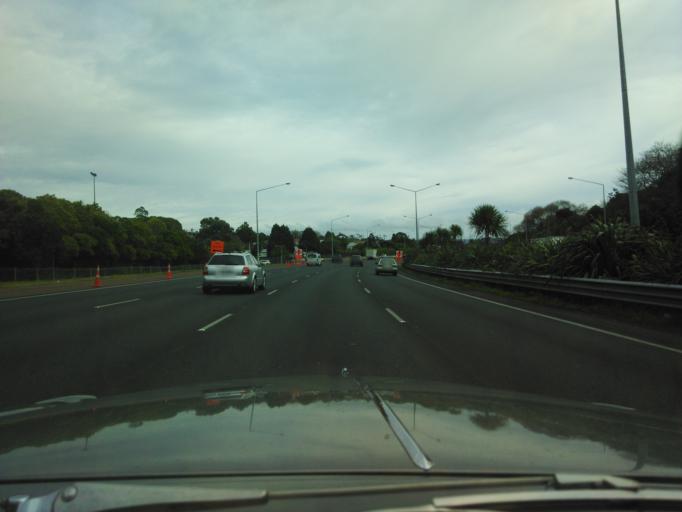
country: NZ
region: Auckland
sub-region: Auckland
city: Auckland
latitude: -36.8686
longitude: 174.7457
